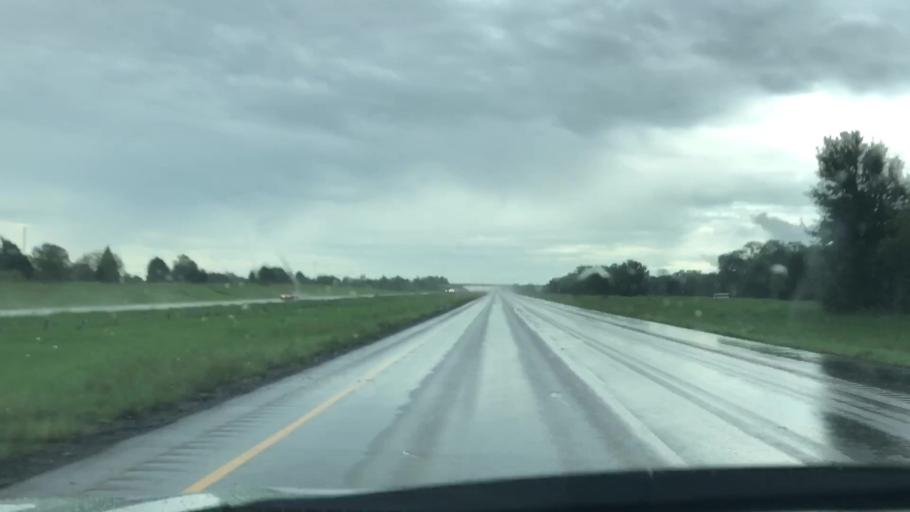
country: US
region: Texas
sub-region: Fayette County
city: Flatonia
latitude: 29.6963
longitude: -97.1368
